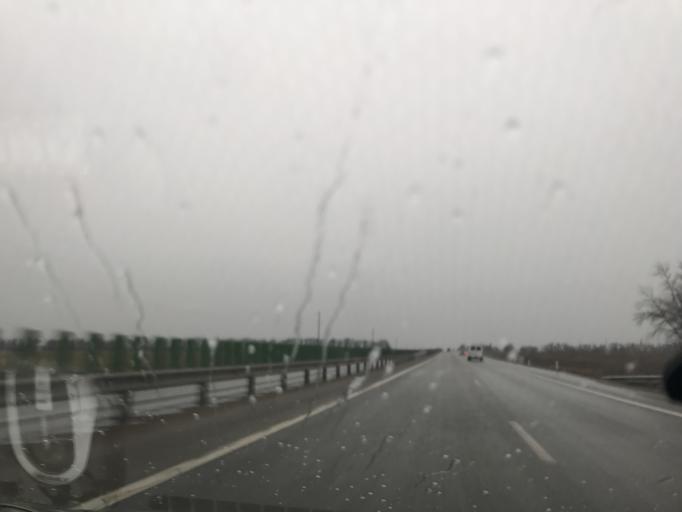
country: RU
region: Krasnodarskiy
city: Kislyakovskaya
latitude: 46.3419
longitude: 39.7795
